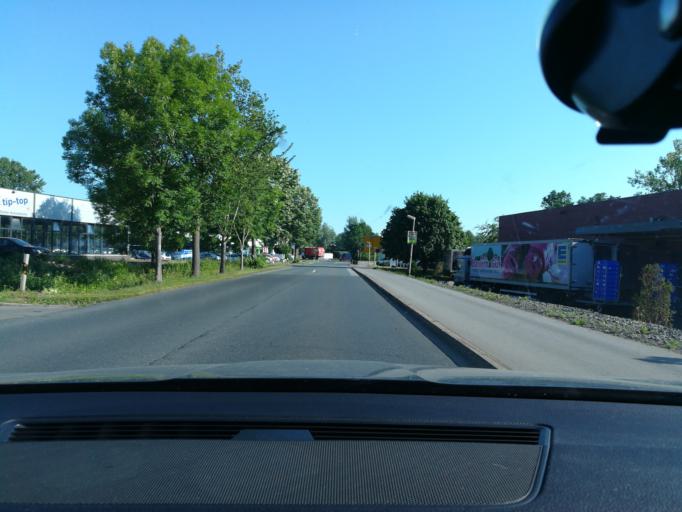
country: DE
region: North Rhine-Westphalia
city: Porta Westfalica
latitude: 52.2616
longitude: 8.8983
